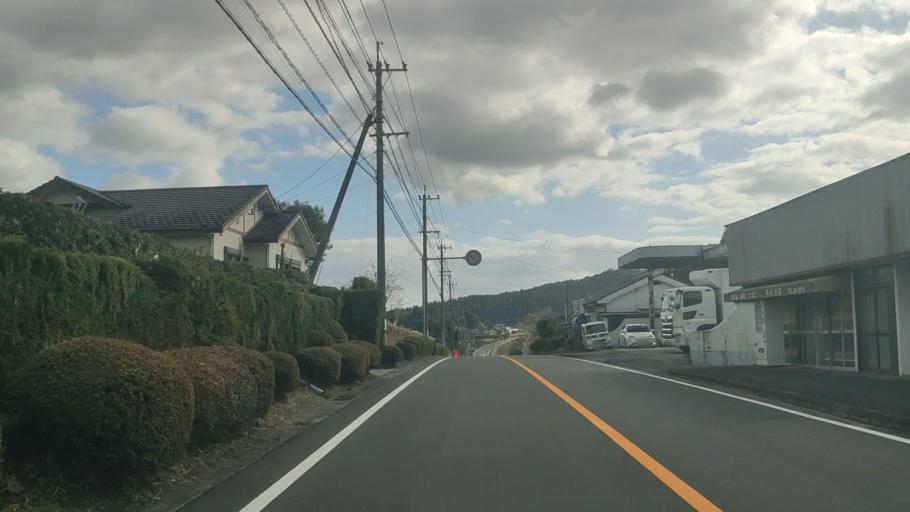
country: JP
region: Kagoshima
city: Kajiki
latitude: 31.8379
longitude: 130.6844
